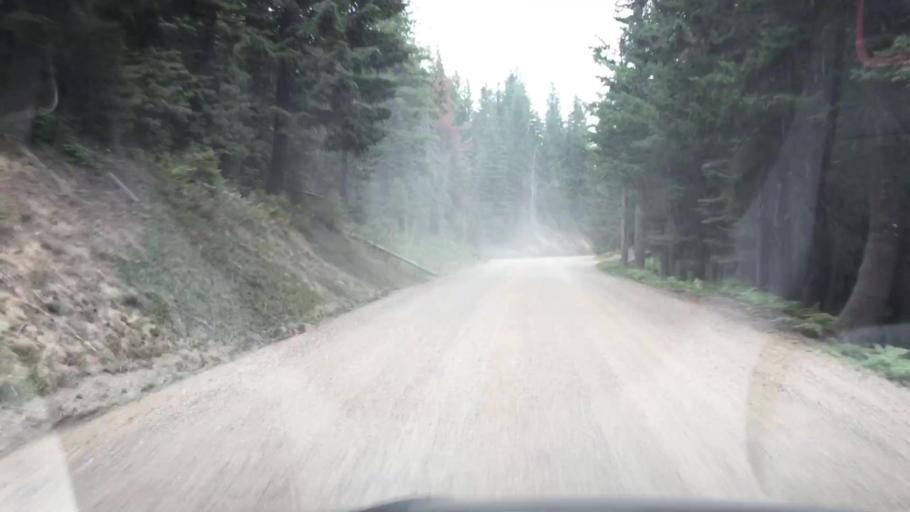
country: US
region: Washington
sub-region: Klickitat County
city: White Salmon
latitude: 46.2603
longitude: -121.6150
